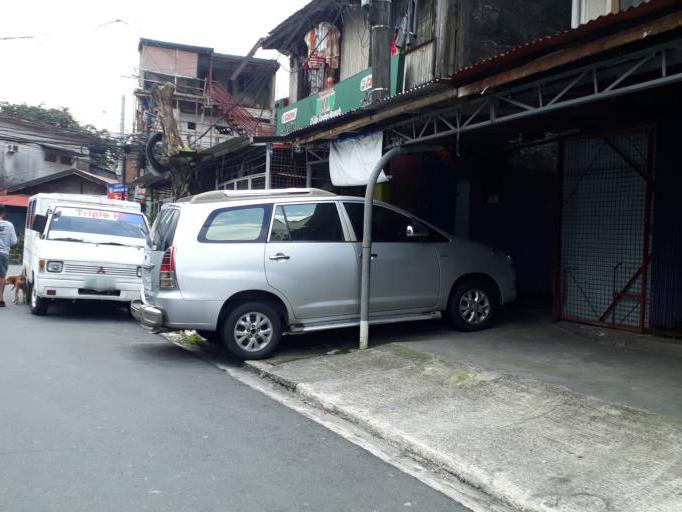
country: PH
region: Calabarzon
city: Bagong Pagasa
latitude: 14.6595
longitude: 121.0243
